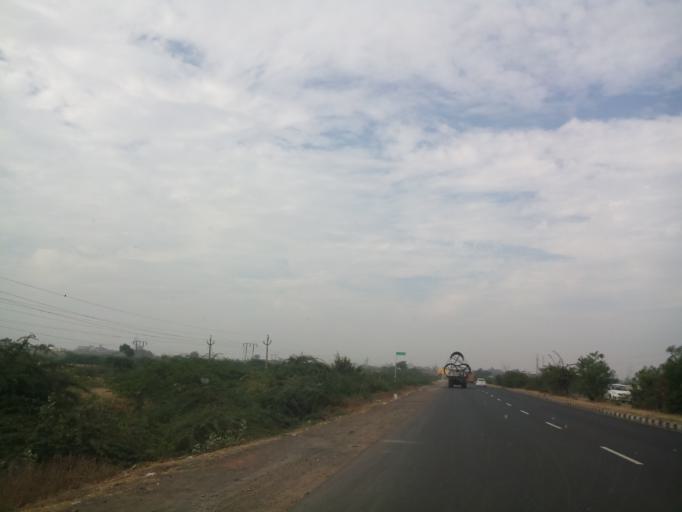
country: IN
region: Gujarat
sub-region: Surendranagar
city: Sayla
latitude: 22.5398
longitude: 71.4965
